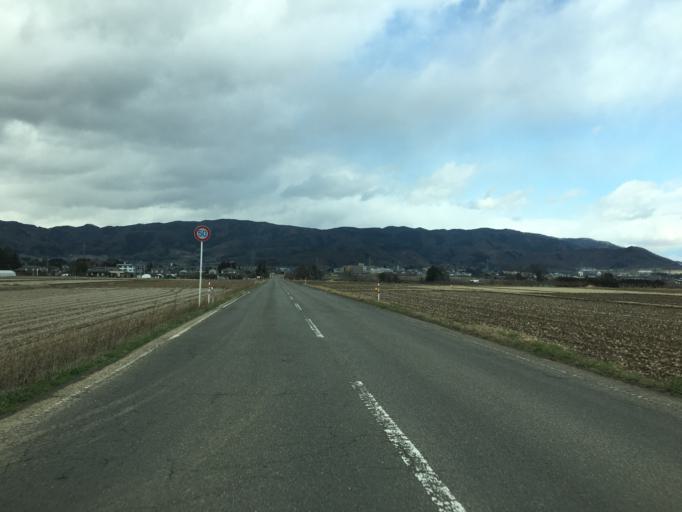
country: JP
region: Fukushima
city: Hobaramachi
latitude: 37.8577
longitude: 140.5381
